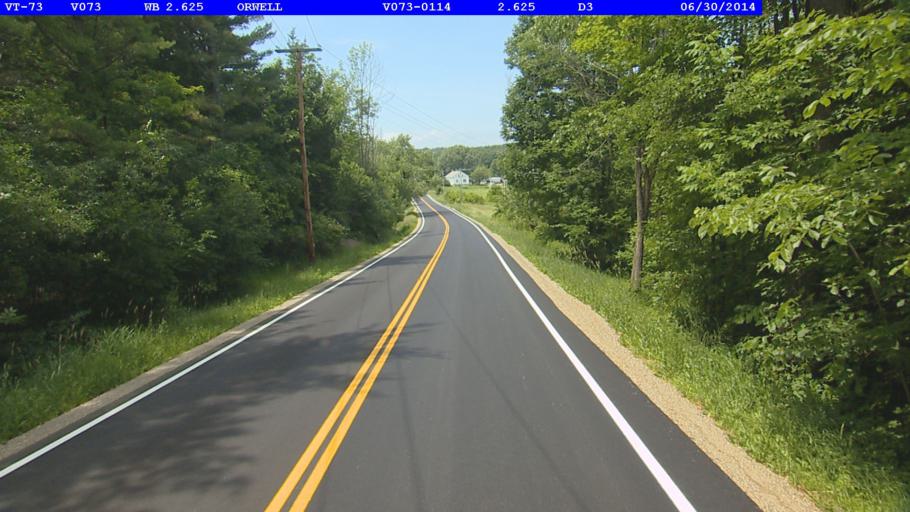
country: US
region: Vermont
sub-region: Rutland County
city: Brandon
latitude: 43.8023
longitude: -73.2546
